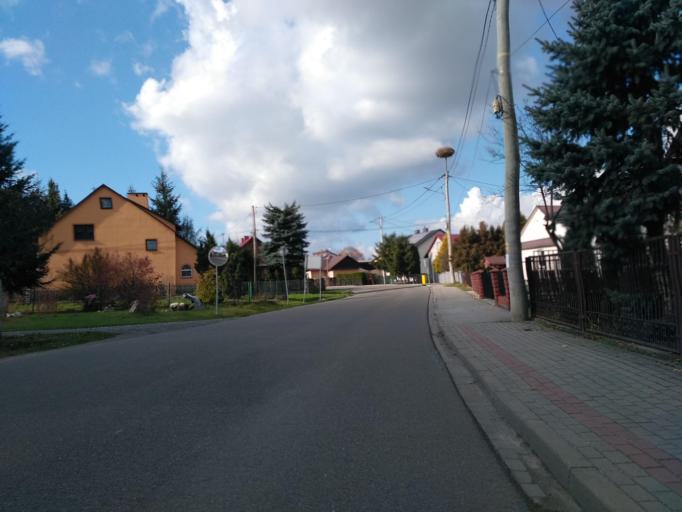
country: PL
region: Subcarpathian Voivodeship
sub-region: Powiat rzeszowski
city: Swilcza
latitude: 50.1142
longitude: 21.8728
